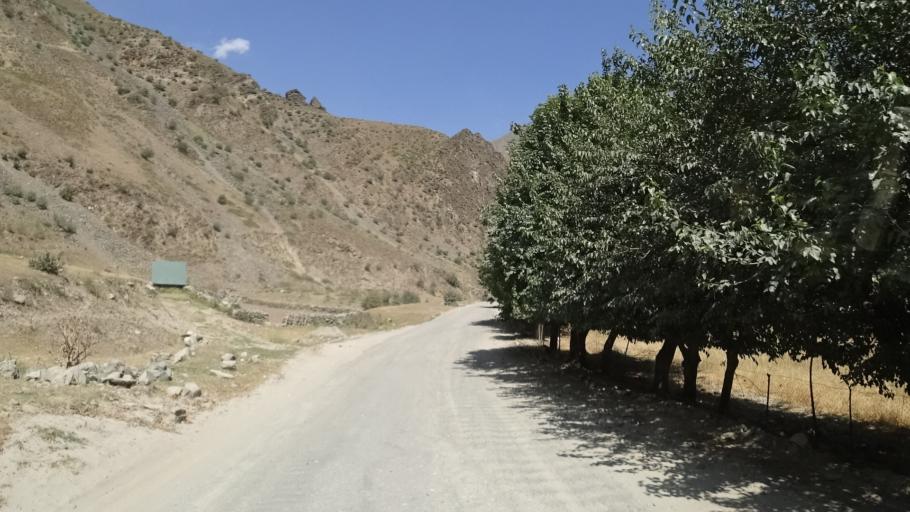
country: AF
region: Badakhshan
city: Maymay
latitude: 38.4437
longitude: 70.9358
